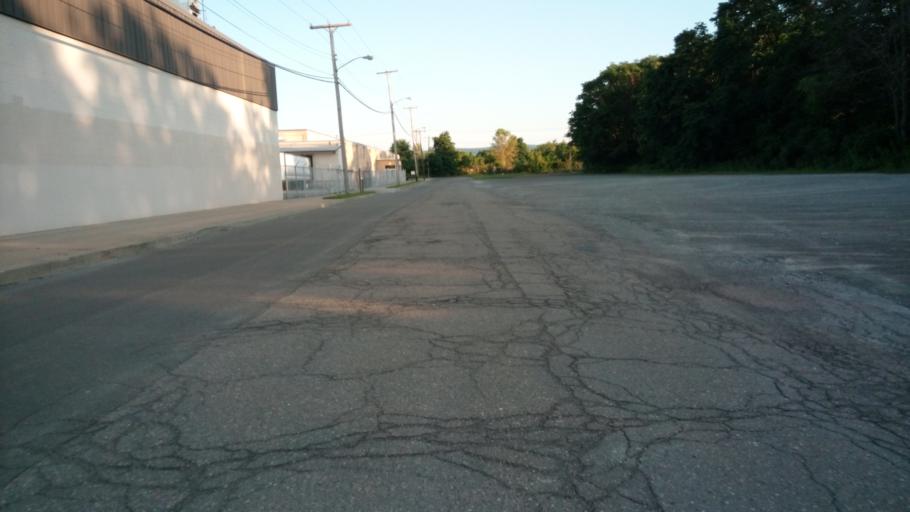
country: US
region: New York
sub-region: Chemung County
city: Elmira
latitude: 42.0983
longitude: -76.8097
